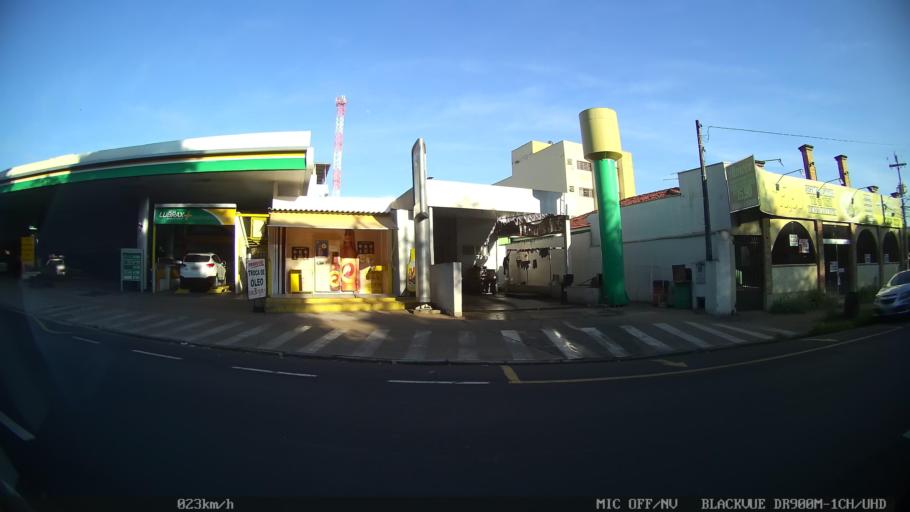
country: BR
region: Sao Paulo
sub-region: Sao Jose Do Rio Preto
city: Sao Jose do Rio Preto
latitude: -20.8196
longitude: -49.3663
